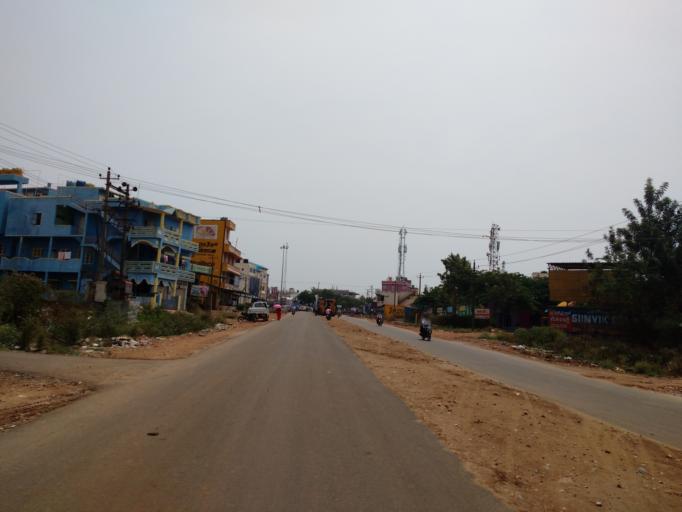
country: IN
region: Karnataka
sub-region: Hassan
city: Hassan
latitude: 13.0265
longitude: 76.1002
